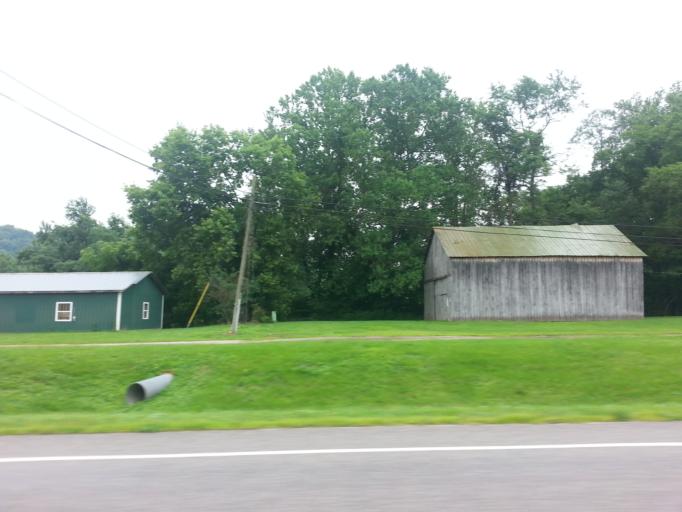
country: US
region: Ohio
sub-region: Brown County
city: Aberdeen
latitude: 38.6885
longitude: -83.7780
